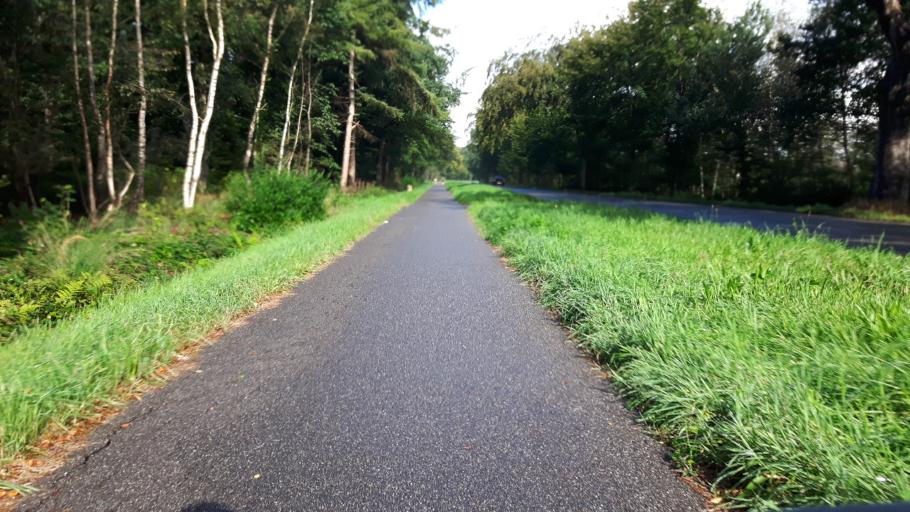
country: NL
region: Friesland
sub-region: Gemeente Smallingerland
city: Drachten
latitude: 53.0716
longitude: 6.1013
